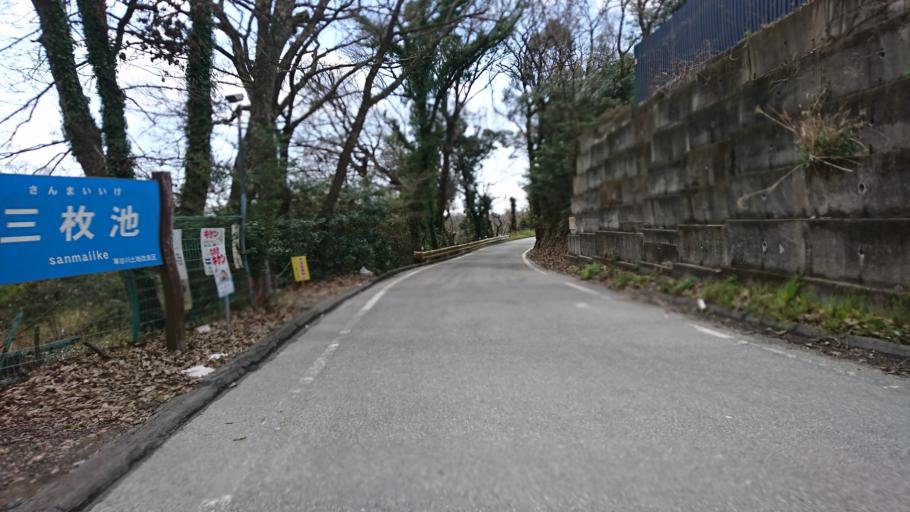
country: JP
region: Hyogo
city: Miki
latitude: 34.7690
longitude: 134.9607
